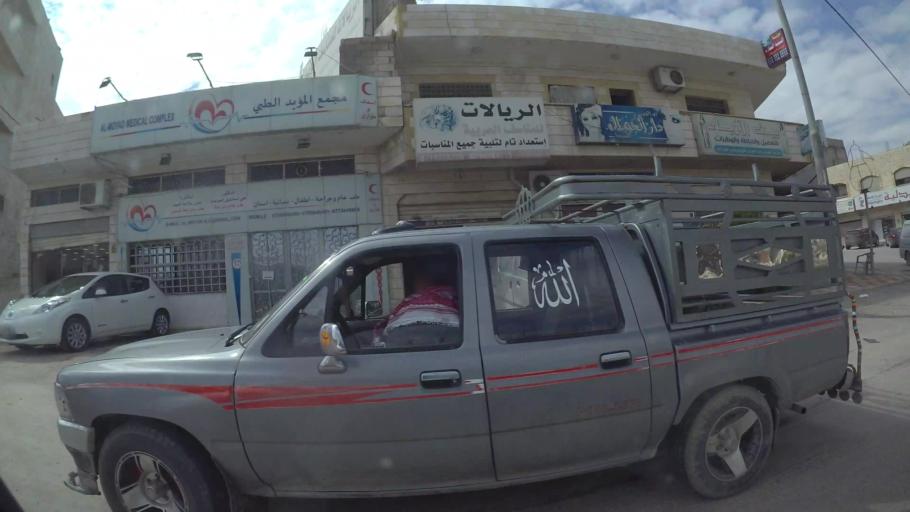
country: JO
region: Amman
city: Al Jubayhah
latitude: 32.0602
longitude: 35.8121
